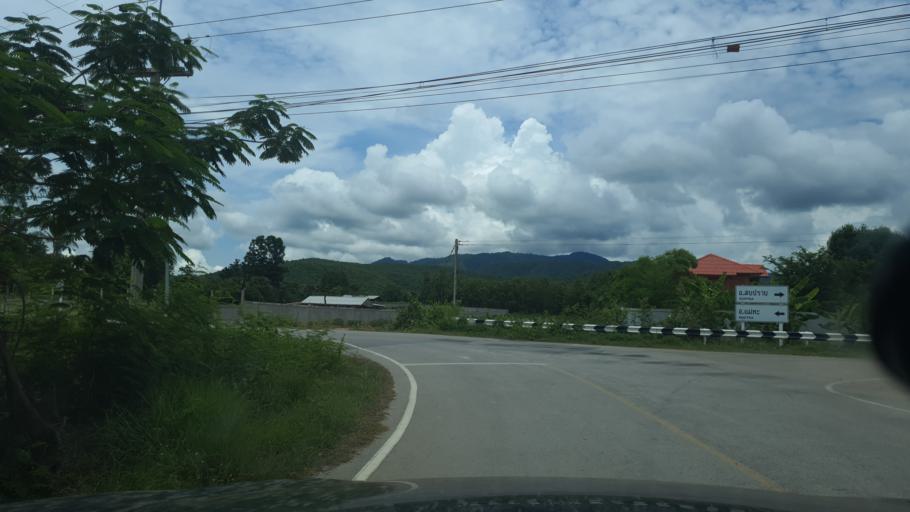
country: TH
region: Lampang
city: Sop Prap
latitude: 17.9211
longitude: 99.4110
